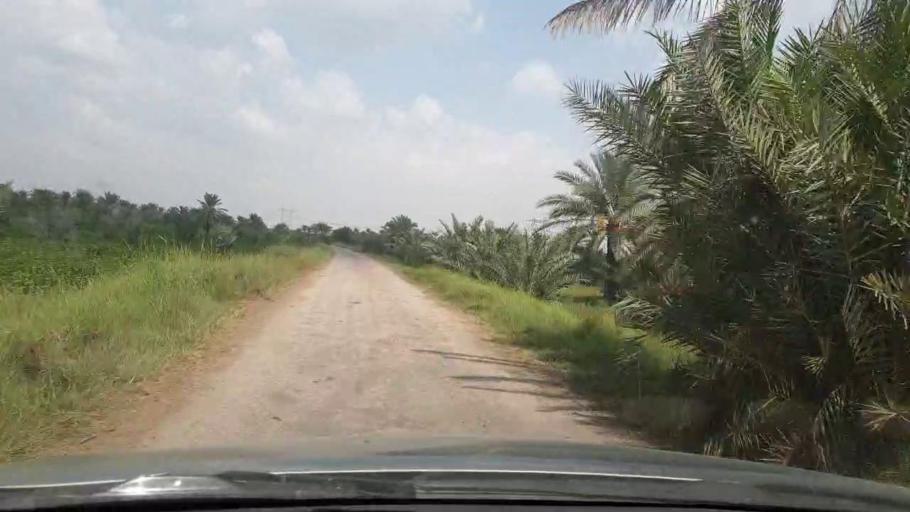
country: PK
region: Sindh
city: Khairpur
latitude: 27.4655
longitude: 68.7603
